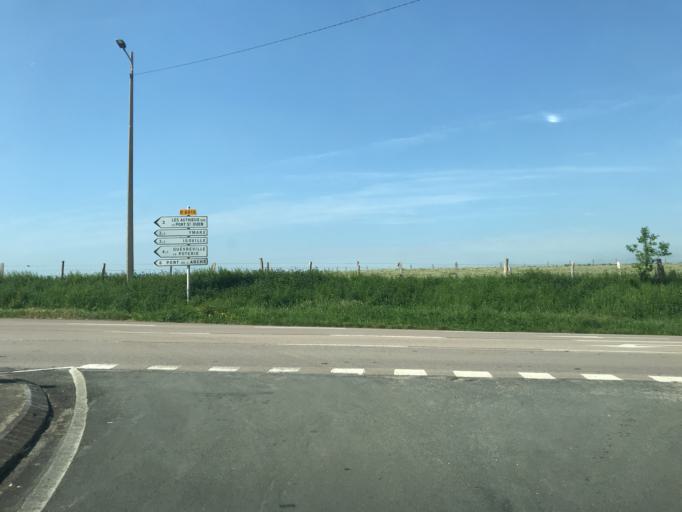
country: FR
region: Haute-Normandie
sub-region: Departement de la Seine-Maritime
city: Les Authieux-sur-le-Port-Saint-Ouen
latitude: 49.3497
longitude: 1.1458
